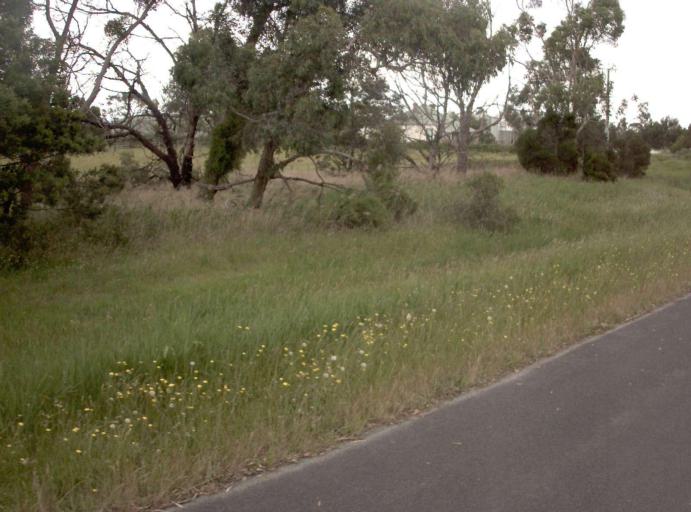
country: AU
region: Victoria
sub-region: Casey
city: Tooradin
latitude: -38.2176
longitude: 145.3979
